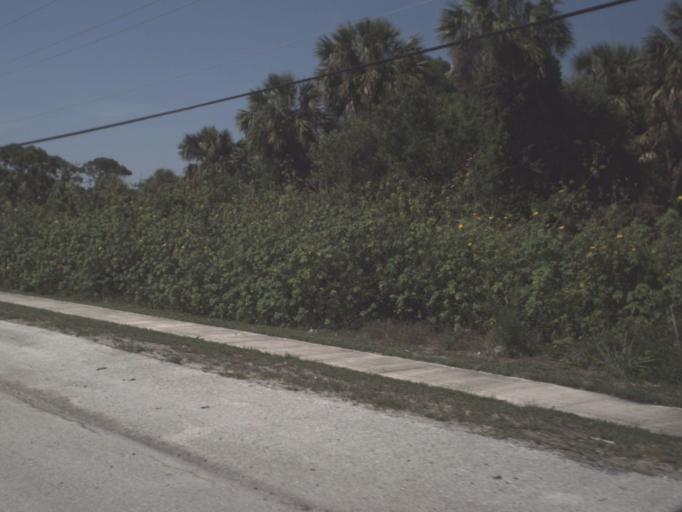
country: US
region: Florida
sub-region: Brevard County
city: South Patrick Shores
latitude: 28.1693
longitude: -80.6458
